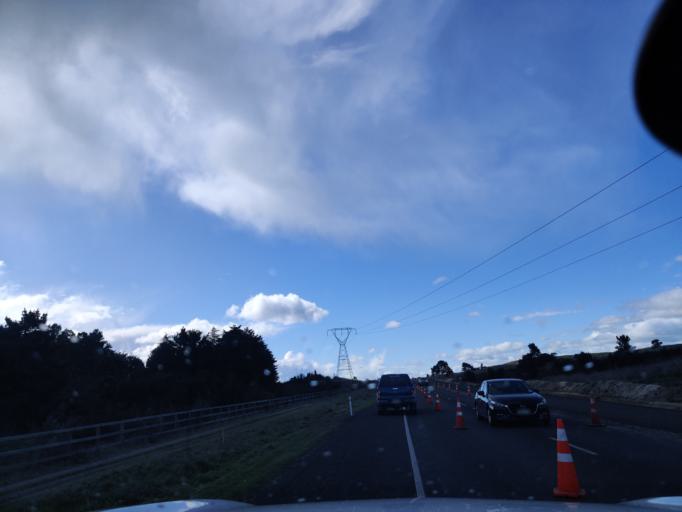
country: NZ
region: Waikato
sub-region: Taupo District
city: Taupo
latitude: -38.6987
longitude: 176.1117
